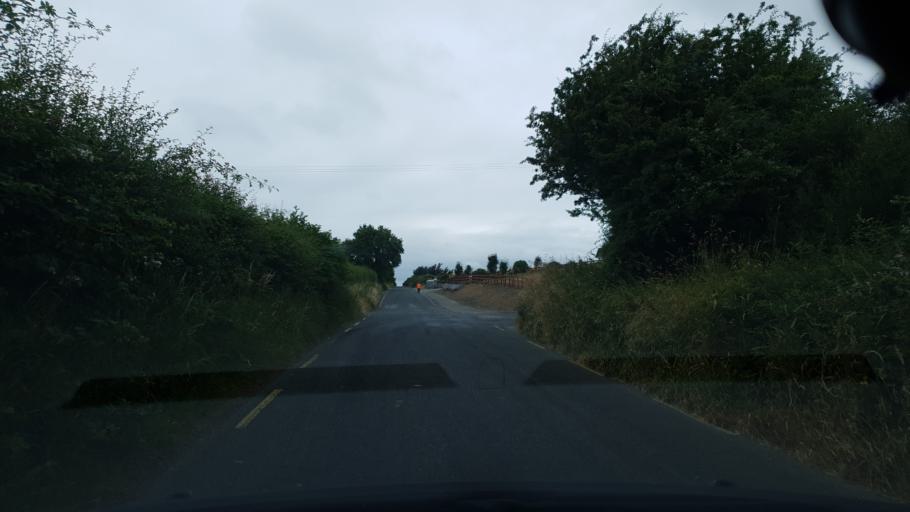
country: IE
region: Munster
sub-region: Ciarrai
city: Cill Airne
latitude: 52.1353
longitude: -9.5820
